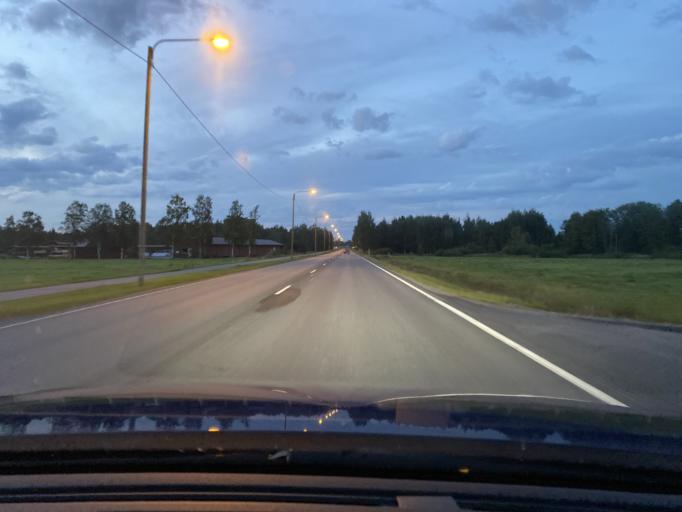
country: FI
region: Southern Ostrobothnia
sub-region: Suupohja
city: Kauhajoki
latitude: 62.4486
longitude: 22.2162
